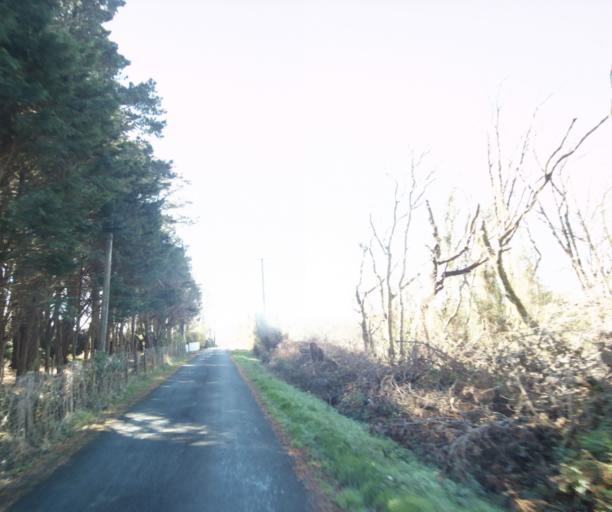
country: FR
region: Aquitaine
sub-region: Departement des Pyrenees-Atlantiques
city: Ciboure
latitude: 43.3878
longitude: -1.6958
